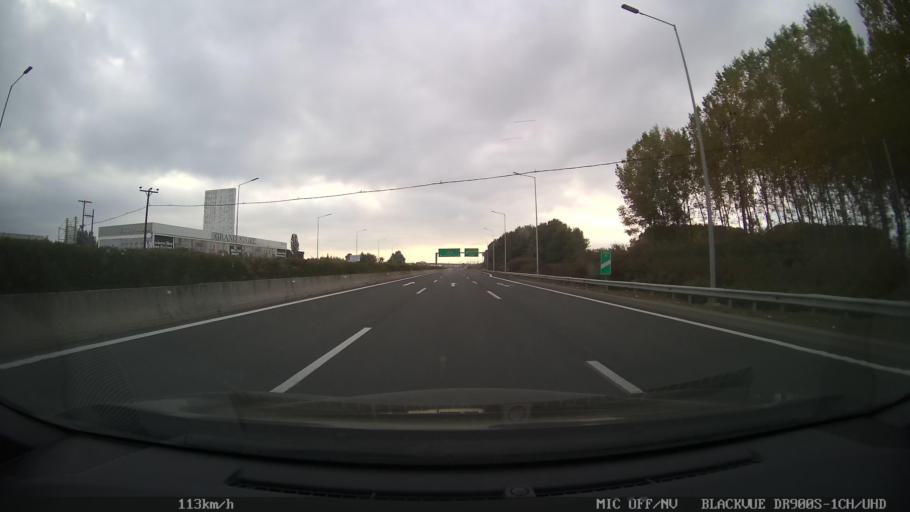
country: GR
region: Central Macedonia
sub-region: Nomos Pierias
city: Nea Efesos
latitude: 40.1994
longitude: 22.5474
